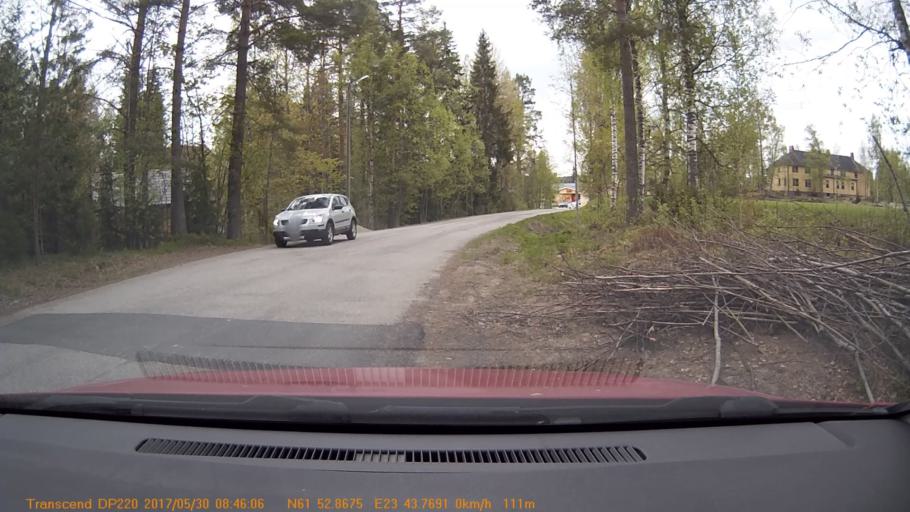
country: FI
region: Pirkanmaa
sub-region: Tampere
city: Kuru
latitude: 61.8811
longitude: 23.7295
